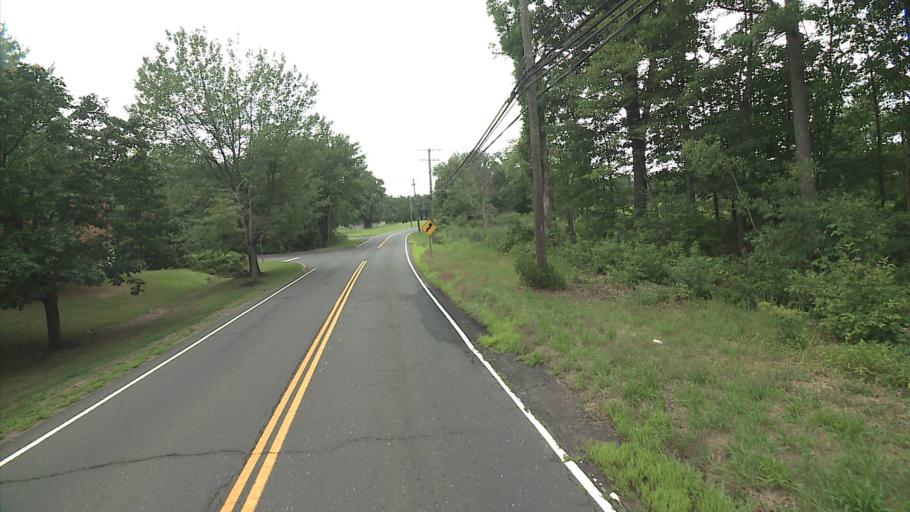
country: US
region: Connecticut
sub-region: Tolland County
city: Rockville
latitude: 41.8650
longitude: -72.4824
